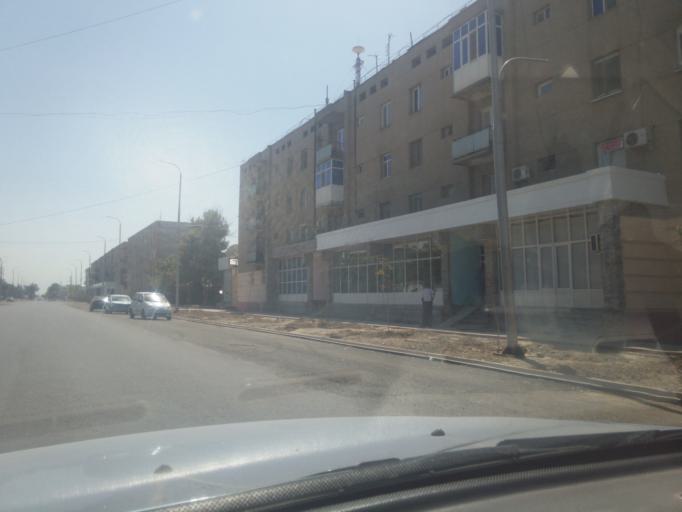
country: UZ
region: Sirdaryo
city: Guliston
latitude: 40.5037
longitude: 68.7748
